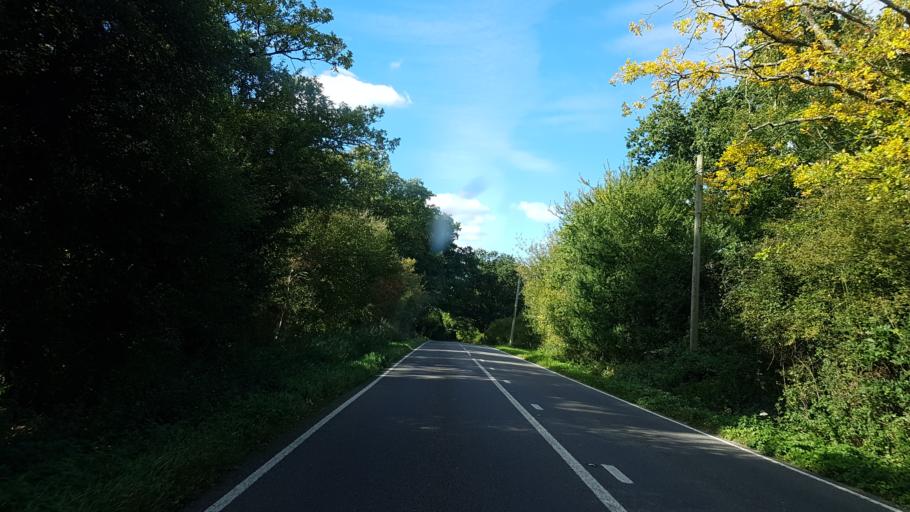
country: GB
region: England
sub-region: West Sussex
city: Petworth
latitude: 50.9981
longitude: -0.6161
